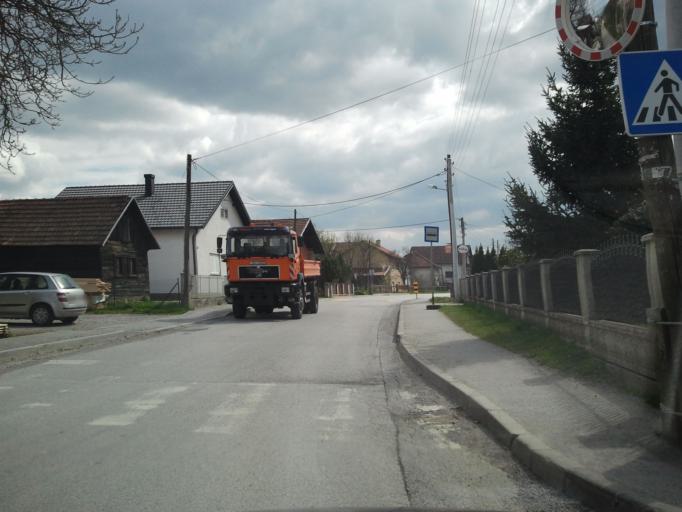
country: HR
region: Grad Zagreb
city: Brezovica
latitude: 45.7321
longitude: 15.8986
